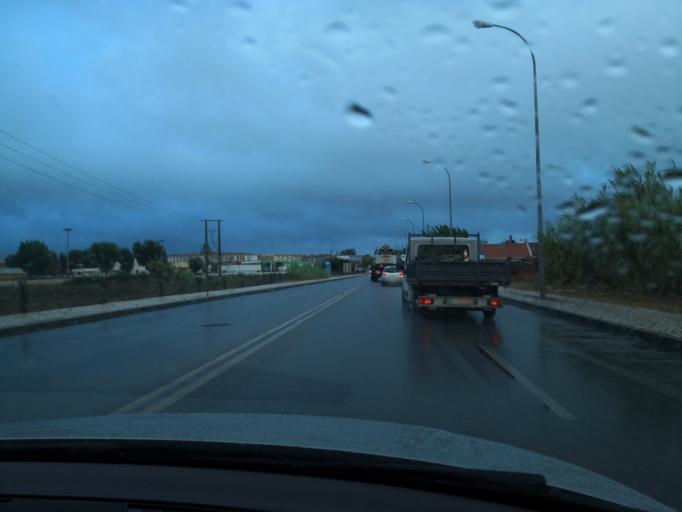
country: PT
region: Setubal
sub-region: Moita
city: Moita
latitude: 38.6487
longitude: -8.9962
